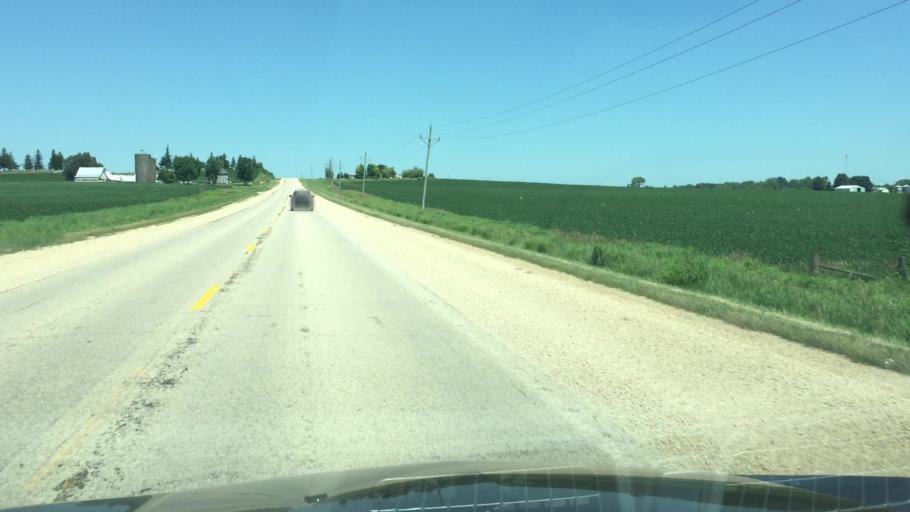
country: US
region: Iowa
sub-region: Cedar County
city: Mechanicsville
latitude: 41.9759
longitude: -91.1418
